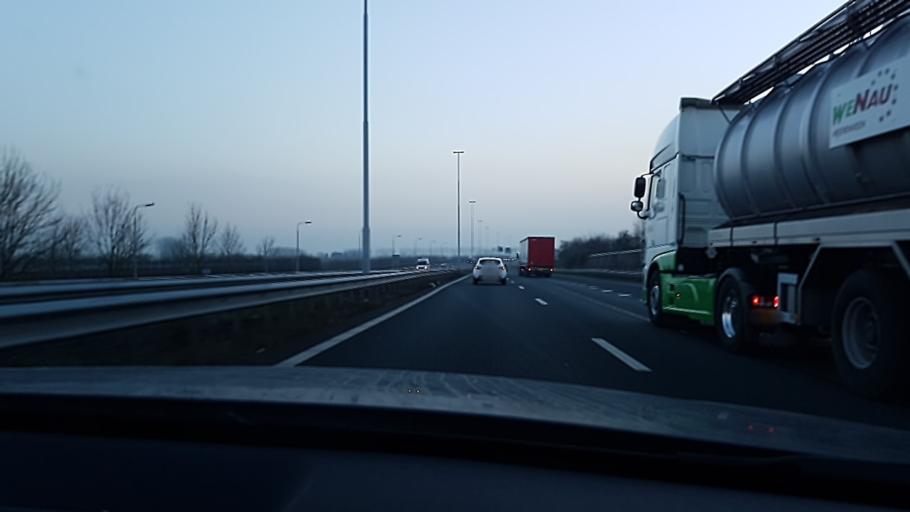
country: NL
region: North Brabant
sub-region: Gemeente Woudrichem
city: Almkerk
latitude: 51.7707
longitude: 4.9278
